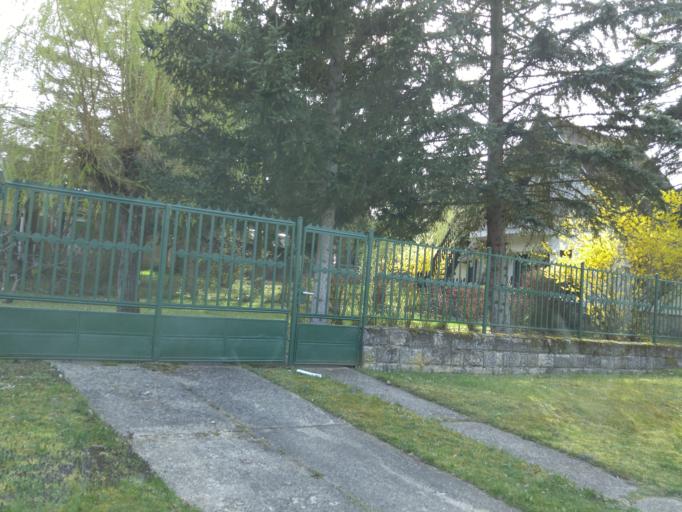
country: HU
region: Nograd
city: Retsag
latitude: 47.9184
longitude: 19.1793
